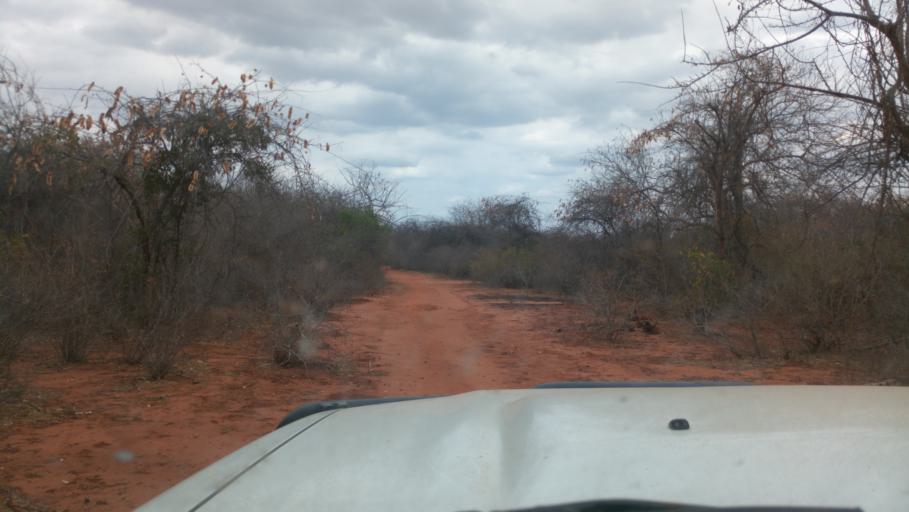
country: KE
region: Kitui
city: Kitui
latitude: -1.7725
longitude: 38.4629
